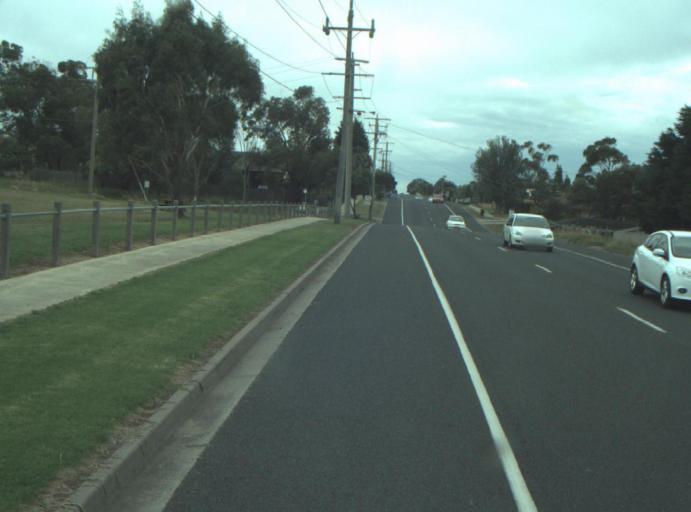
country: AU
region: Victoria
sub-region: Greater Geelong
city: Leopold
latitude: -38.1779
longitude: 144.4667
